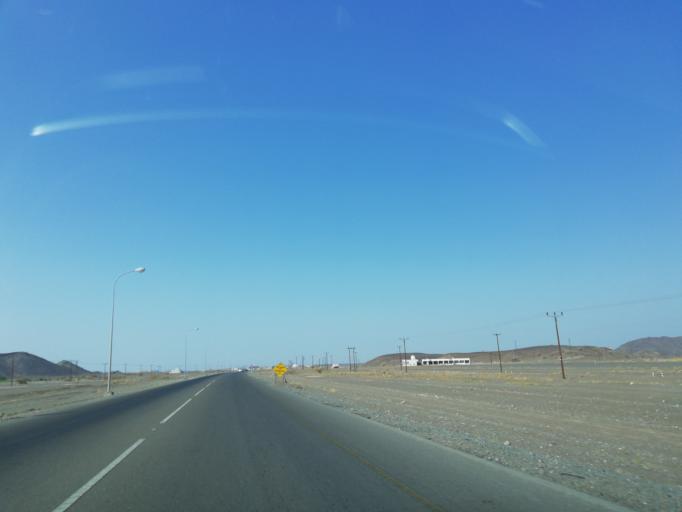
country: OM
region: Ash Sharqiyah
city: Ibra'
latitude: 22.7197
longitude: 58.1481
